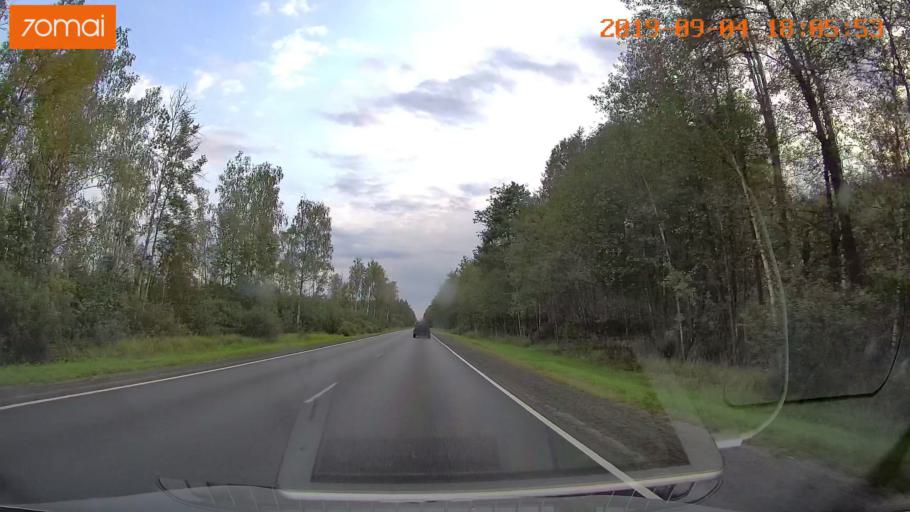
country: RU
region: Moskovskaya
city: Il'inskiy Pogost
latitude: 55.4366
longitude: 38.8211
